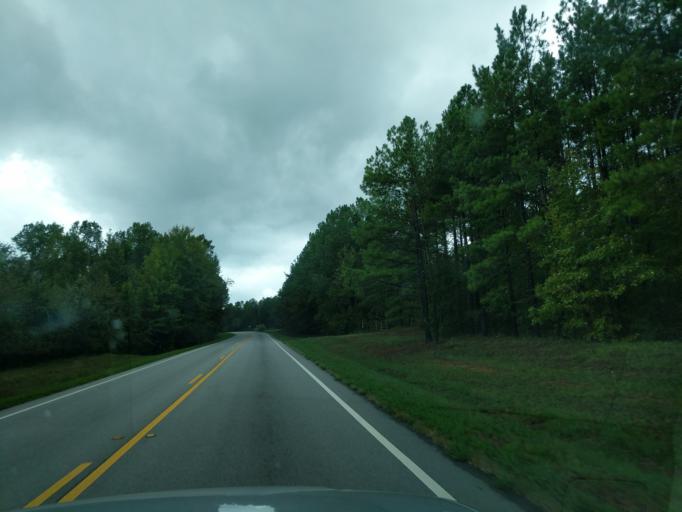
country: US
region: Georgia
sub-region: Elbert County
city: Elberton
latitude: 33.9501
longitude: -82.7698
